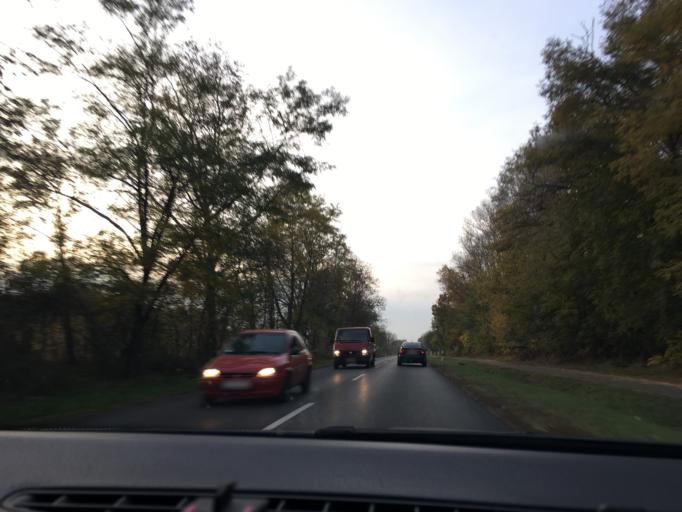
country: HU
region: Szabolcs-Szatmar-Bereg
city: Nagykallo
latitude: 47.8637
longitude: 21.8867
